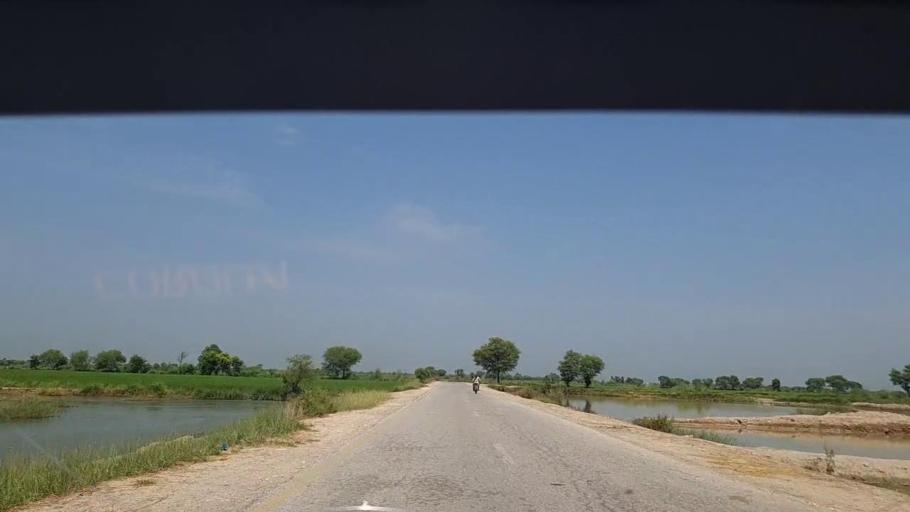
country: PK
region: Sindh
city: Thul
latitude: 28.1303
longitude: 68.8178
